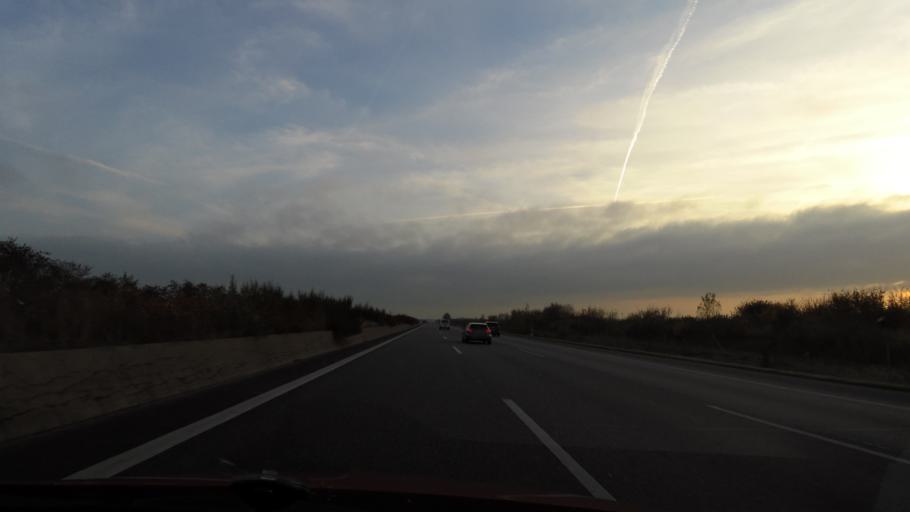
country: DE
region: Saxony-Anhalt
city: Thalheim
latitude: 51.6678
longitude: 12.2046
